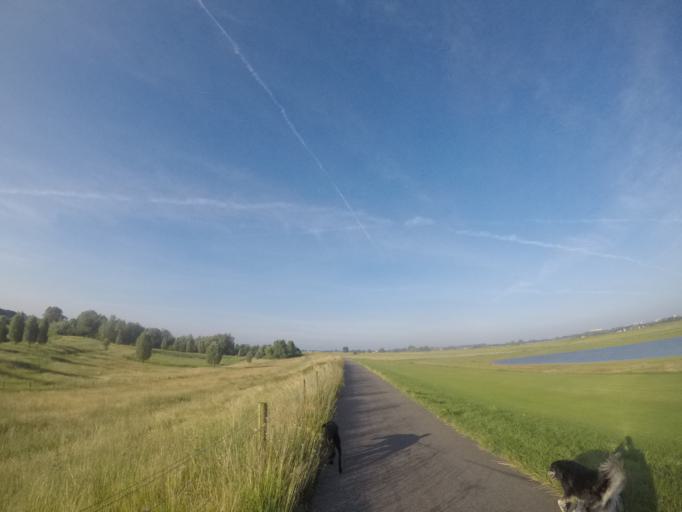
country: NL
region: Gelderland
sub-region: Gemeente Westervoort
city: Westervoort
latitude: 51.9615
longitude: 5.9563
